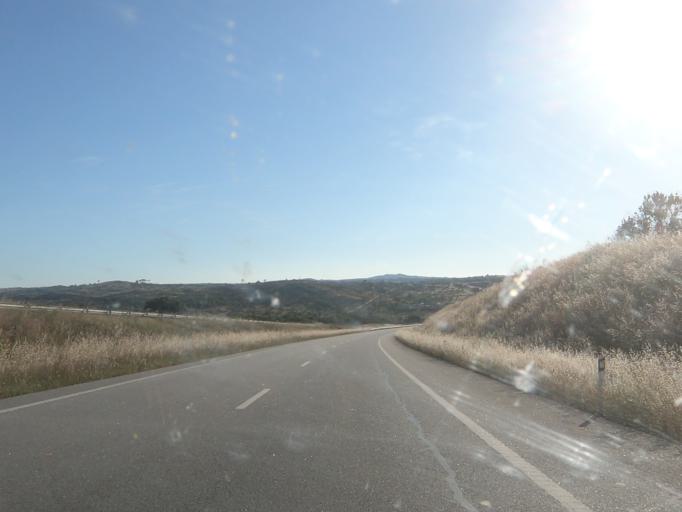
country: PT
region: Guarda
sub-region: Pinhel
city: Pinhel
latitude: 40.6050
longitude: -7.0212
